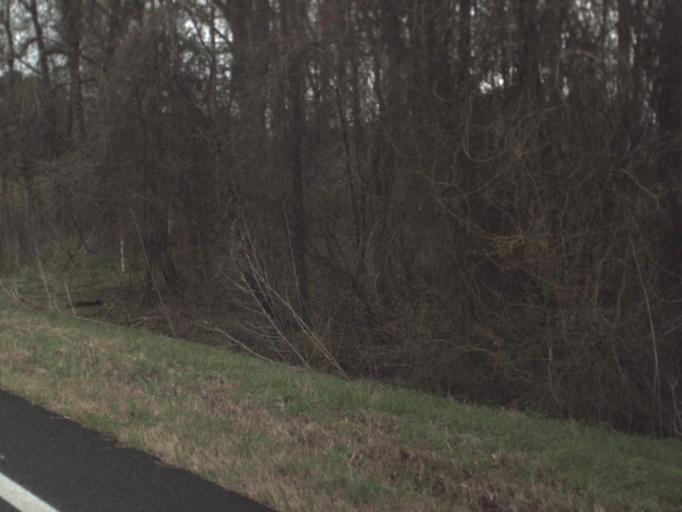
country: US
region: Florida
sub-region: Jefferson County
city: Monticello
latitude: 30.3868
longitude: -83.8384
